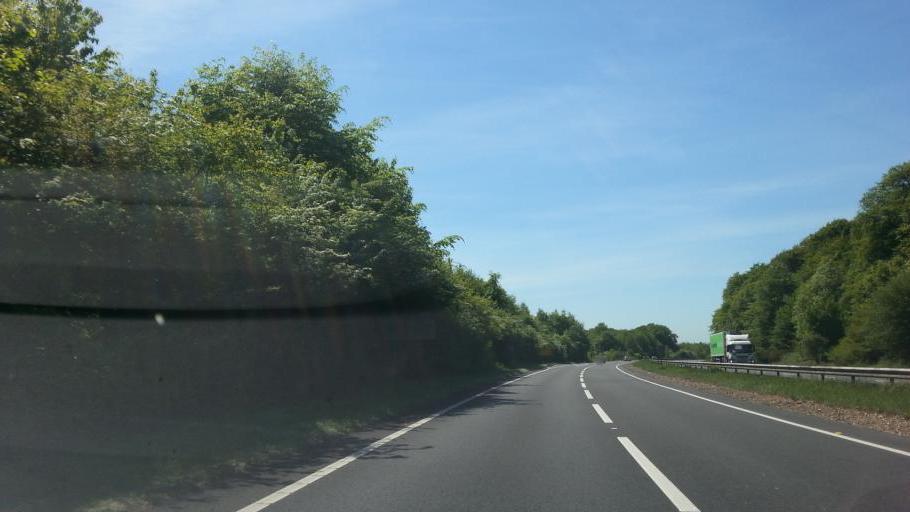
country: GB
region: England
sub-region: Hampshire
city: Overton
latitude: 51.1902
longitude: -1.2499
